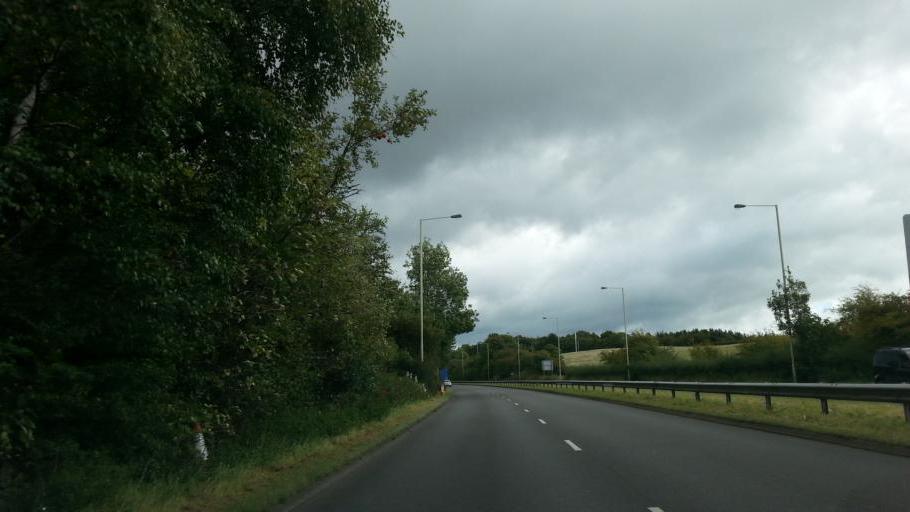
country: GB
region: England
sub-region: Dudley
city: Halesowen
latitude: 52.4479
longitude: -2.0231
